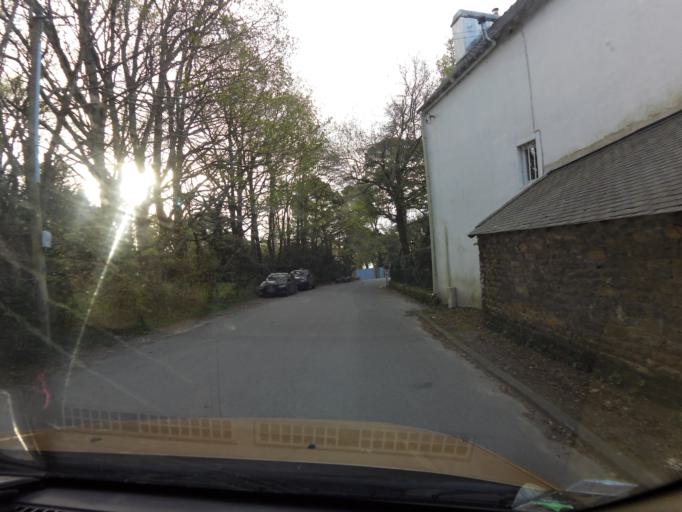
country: FR
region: Brittany
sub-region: Departement du Morbihan
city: Arradon
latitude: 47.6234
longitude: -2.8135
